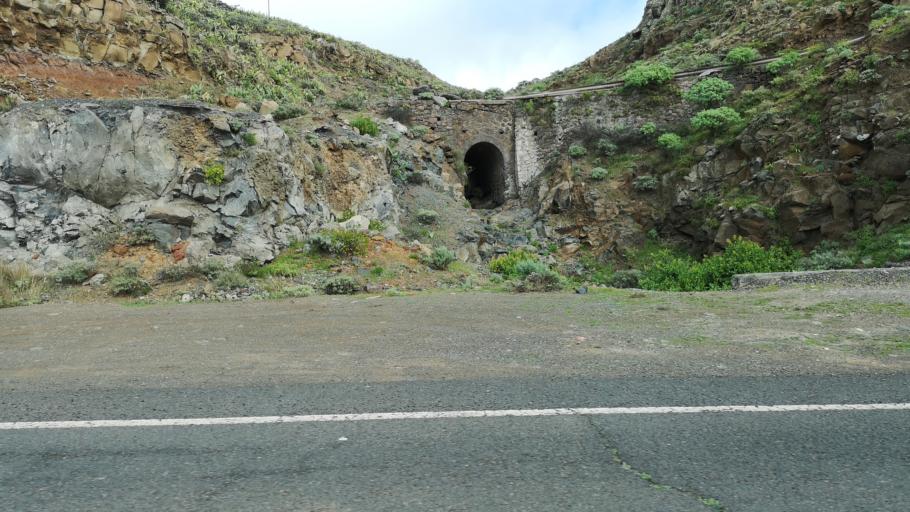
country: ES
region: Canary Islands
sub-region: Provincia de Santa Cruz de Tenerife
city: Vallehermosa
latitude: 28.1259
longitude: -17.3213
